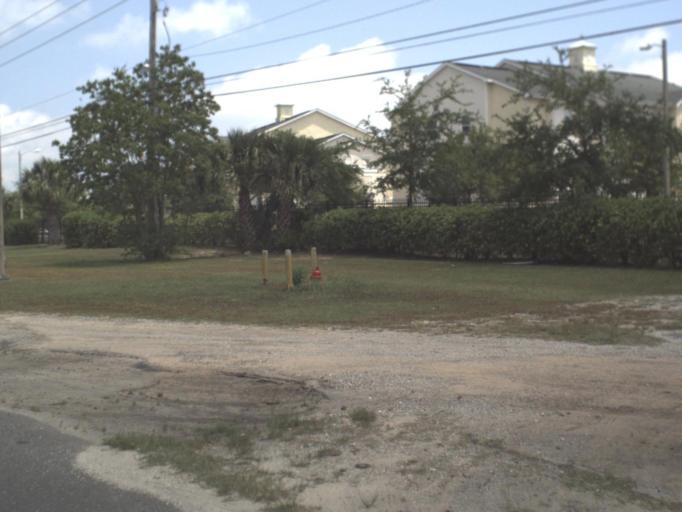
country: US
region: Florida
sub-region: Escambia County
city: West Pensacola
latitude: 30.4072
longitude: -87.2734
